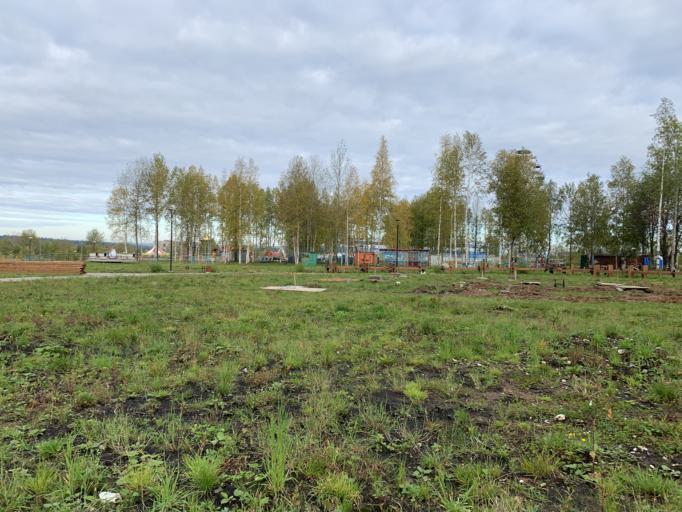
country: RU
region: Perm
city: Gubakha
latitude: 58.8324
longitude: 57.5643
